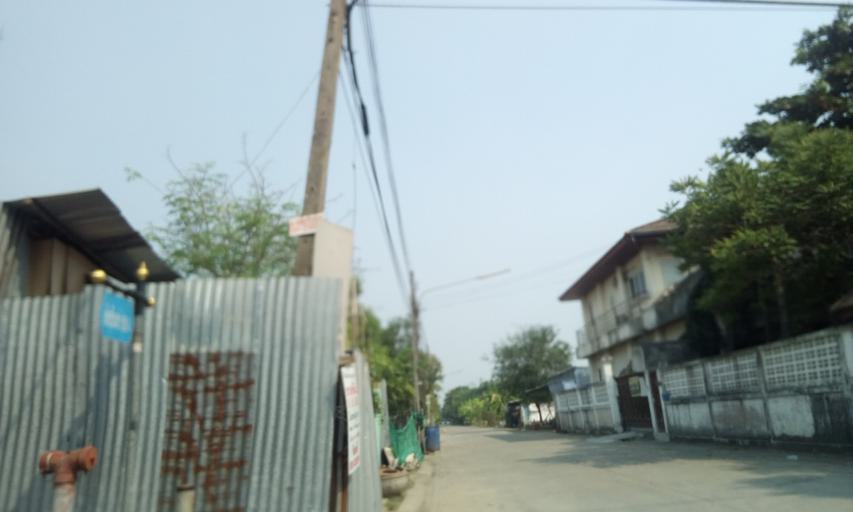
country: TH
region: Pathum Thani
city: Lam Luk Ka
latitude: 13.9372
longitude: 100.7203
